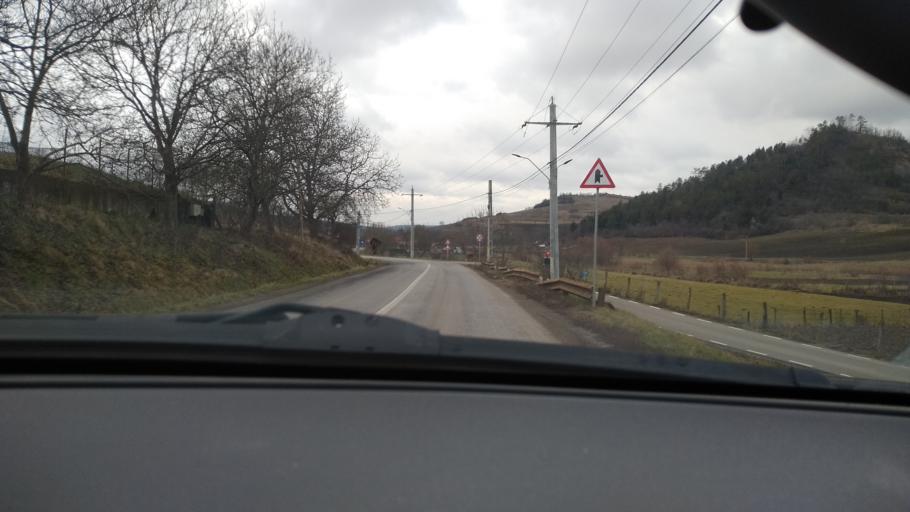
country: RO
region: Mures
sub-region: Comuna Pasareni
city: Pasareni
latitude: 46.5418
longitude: 24.6941
